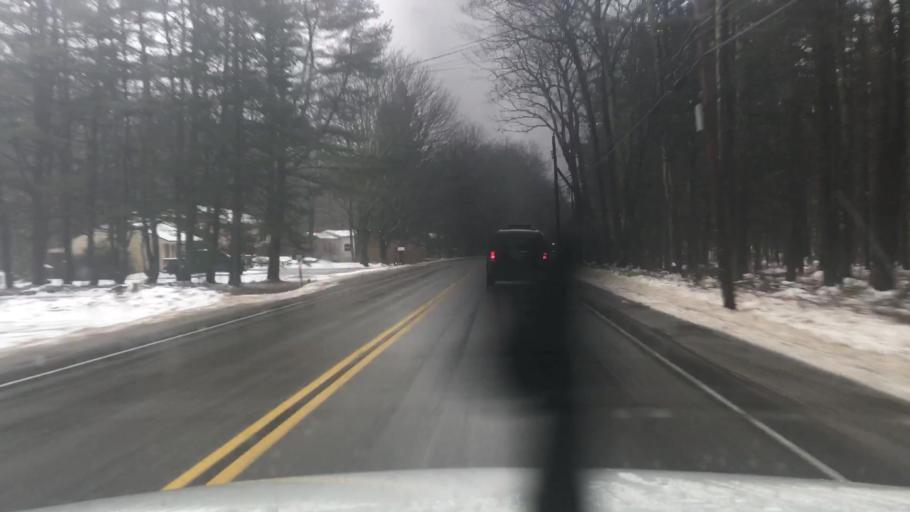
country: US
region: Maine
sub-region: Cumberland County
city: Westbrook
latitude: 43.6382
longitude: -70.3956
